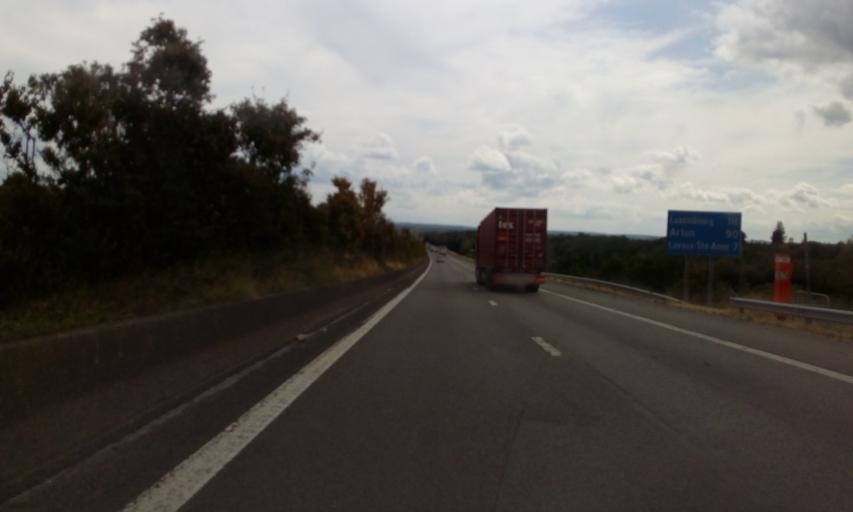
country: BE
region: Wallonia
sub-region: Province de Namur
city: Houyet
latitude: 50.1625
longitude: 5.0712
